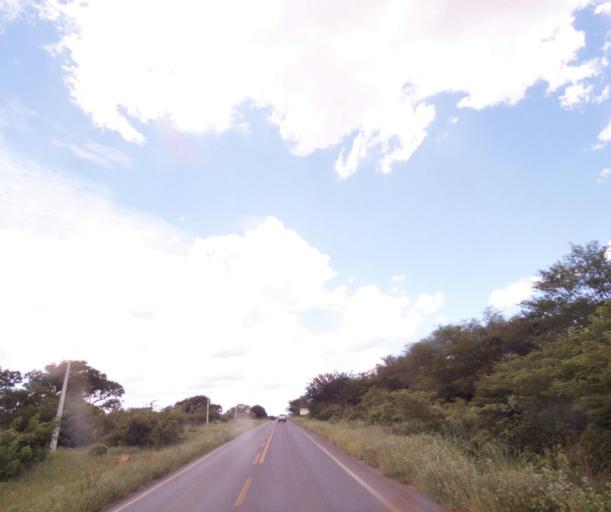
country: BR
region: Bahia
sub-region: Sao Felix Do Coribe
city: Santa Maria da Vitoria
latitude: -13.4078
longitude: -44.1747
